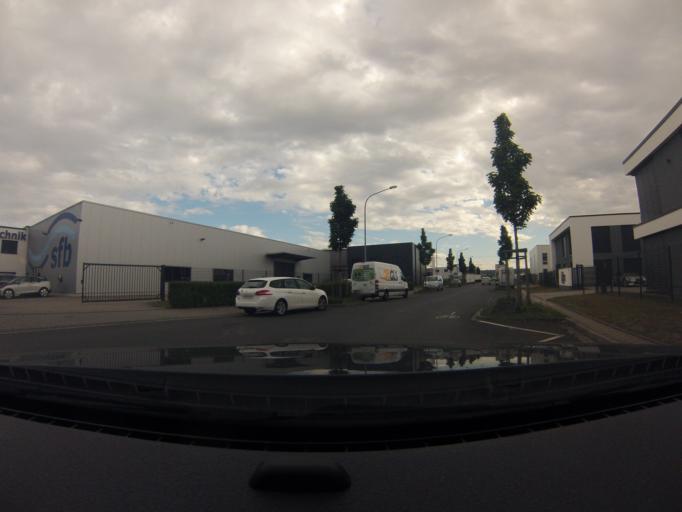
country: DE
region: North Rhine-Westphalia
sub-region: Regierungsbezirk Koln
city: Alfter
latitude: 50.7569
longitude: 7.0318
